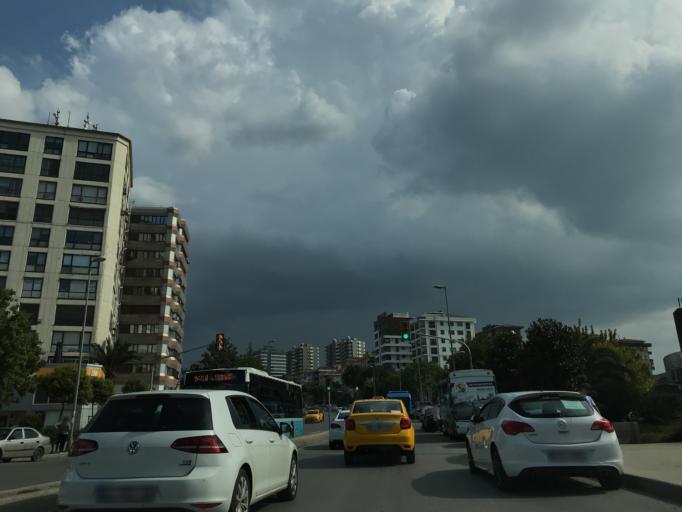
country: TR
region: Istanbul
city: UEskuedar
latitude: 40.9918
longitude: 29.0391
